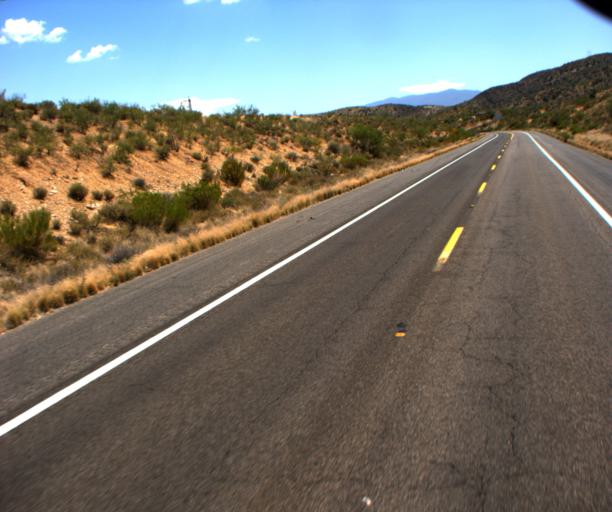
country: US
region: Arizona
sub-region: Gila County
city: Claypool
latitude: 33.4758
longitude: -110.8557
